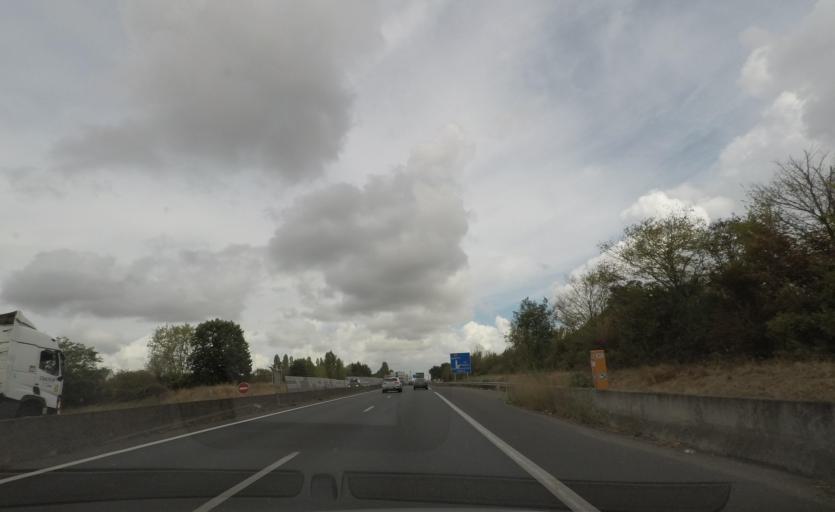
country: FR
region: Pays de la Loire
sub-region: Departement de Maine-et-Loire
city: Ecouflant
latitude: 47.4949
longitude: -0.4983
